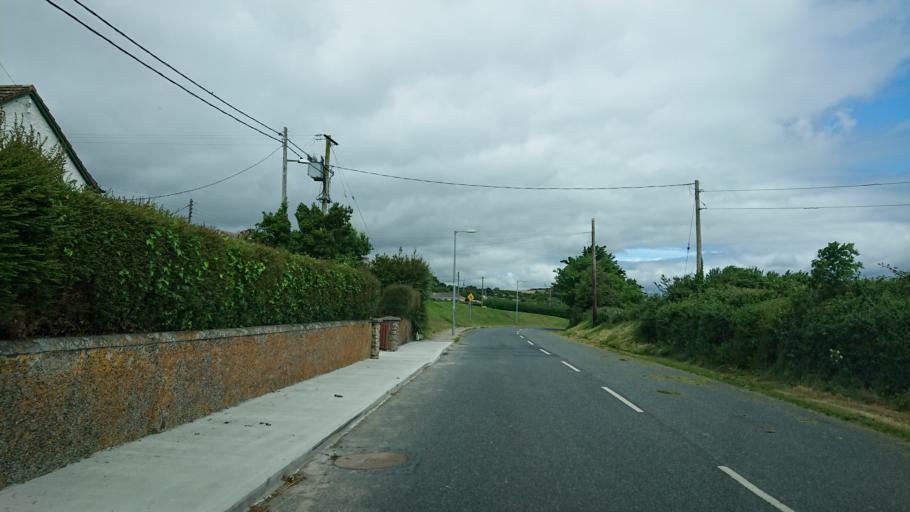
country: IE
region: Munster
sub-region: Waterford
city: Dunmore East
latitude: 52.2298
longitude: -6.9740
